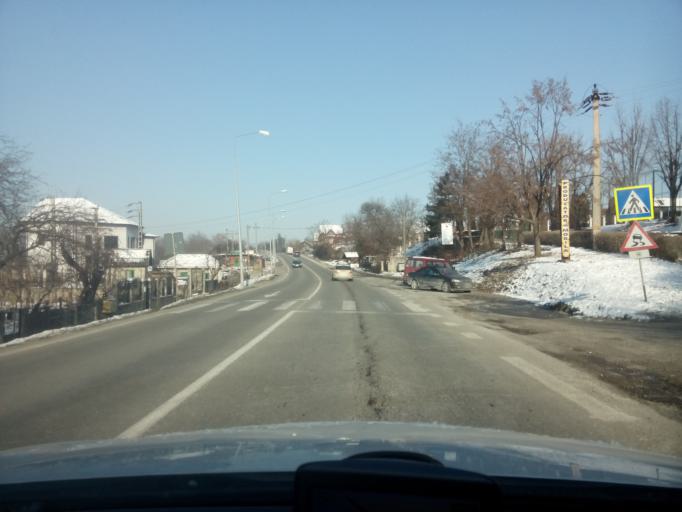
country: RO
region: Valcea
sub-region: Municipiul Ramnicu Valcea
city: Goranu
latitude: 45.1072
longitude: 24.3866
